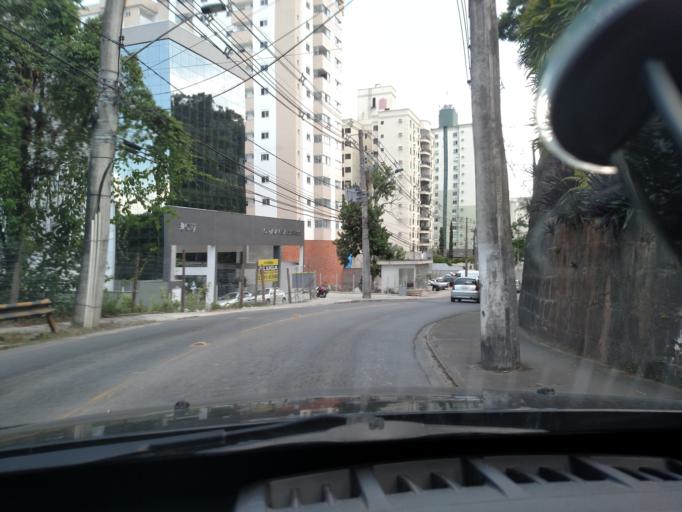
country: BR
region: Santa Catarina
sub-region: Blumenau
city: Blumenau
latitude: -26.9321
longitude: -49.0635
